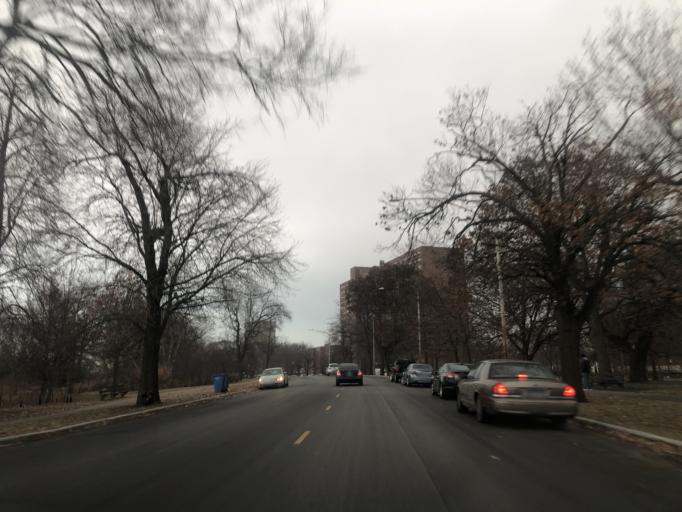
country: US
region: Illinois
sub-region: Cook County
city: Chicago
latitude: 41.7864
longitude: -87.6102
